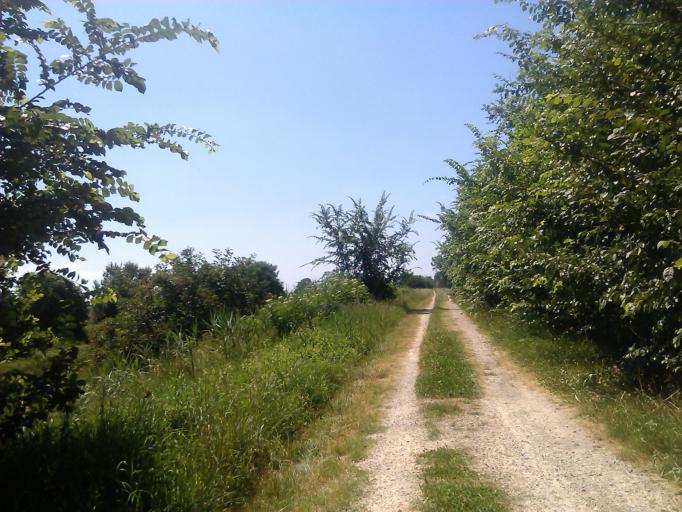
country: IT
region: Tuscany
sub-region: Province of Arezzo
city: Cesa
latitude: 43.3431
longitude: 11.8268
